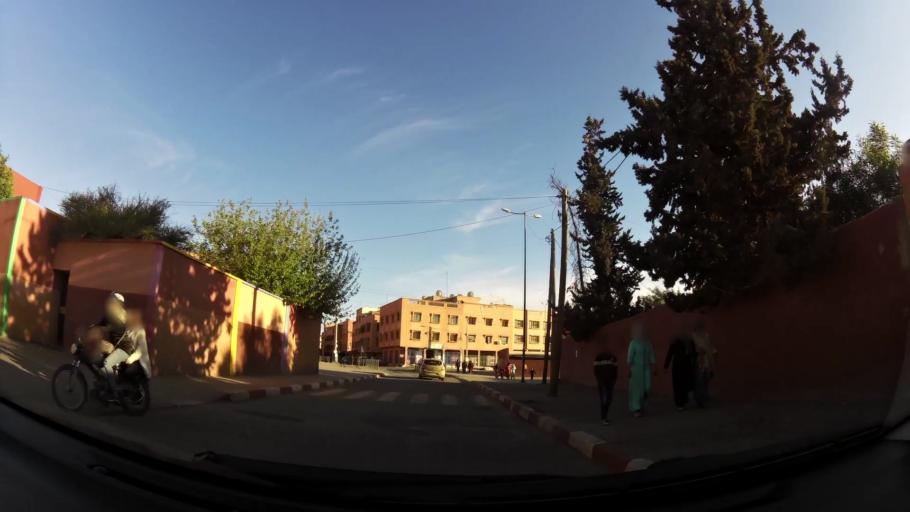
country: MA
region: Marrakech-Tensift-Al Haouz
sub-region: Marrakech
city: Marrakesh
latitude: 31.6202
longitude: -8.0519
